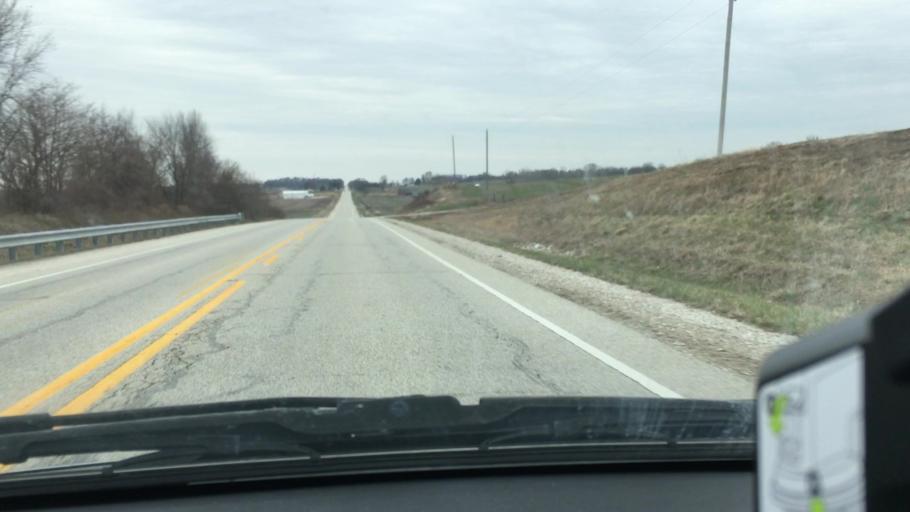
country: US
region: Indiana
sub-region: Greene County
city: Bloomfield
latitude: 38.9664
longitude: -87.0167
